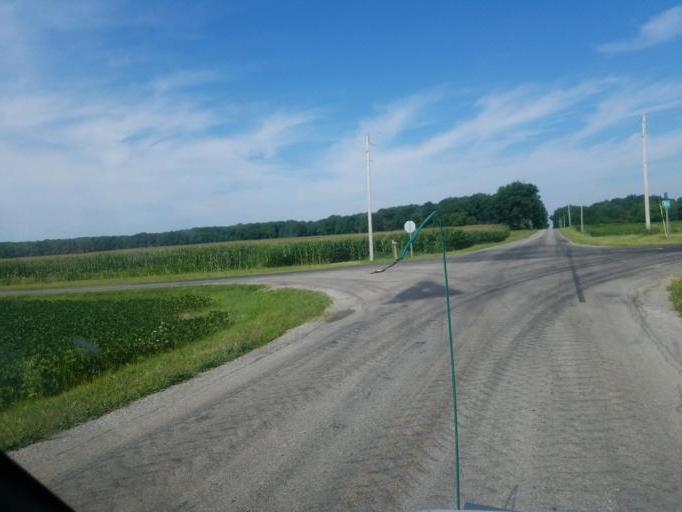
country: US
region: Ohio
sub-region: Hardin County
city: Kenton
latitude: 40.5554
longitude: -83.6360
